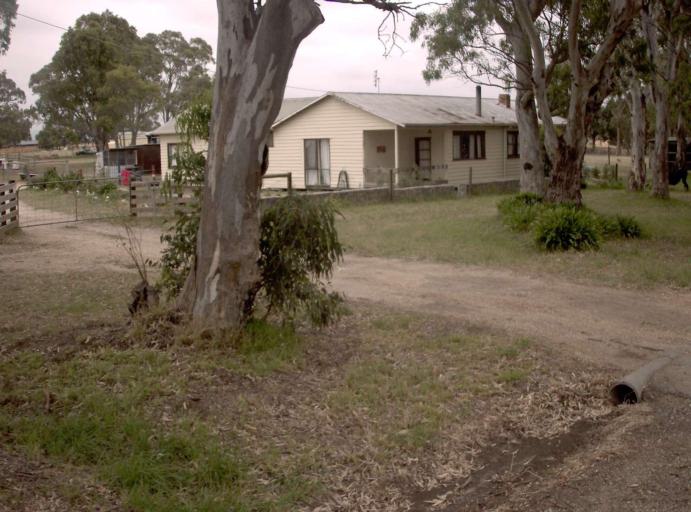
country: AU
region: Victoria
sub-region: Wellington
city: Heyfield
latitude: -37.9747
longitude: 146.7820
